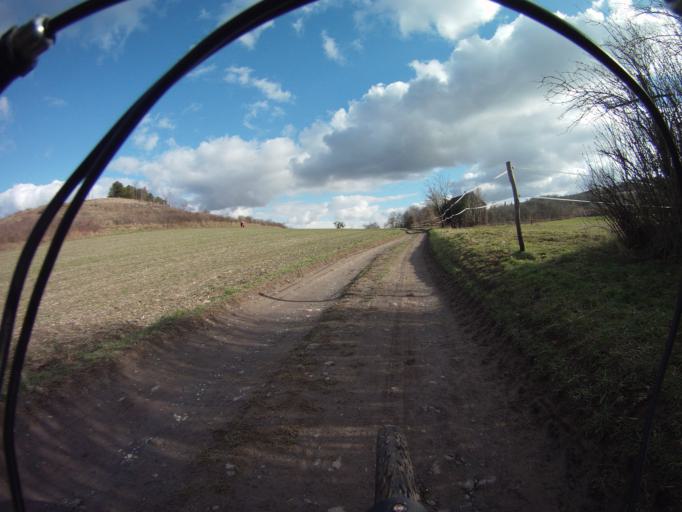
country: FR
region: Auvergne
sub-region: Departement du Puy-de-Dome
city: Perignat-les-Sarlieve
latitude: 45.7372
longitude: 3.1312
